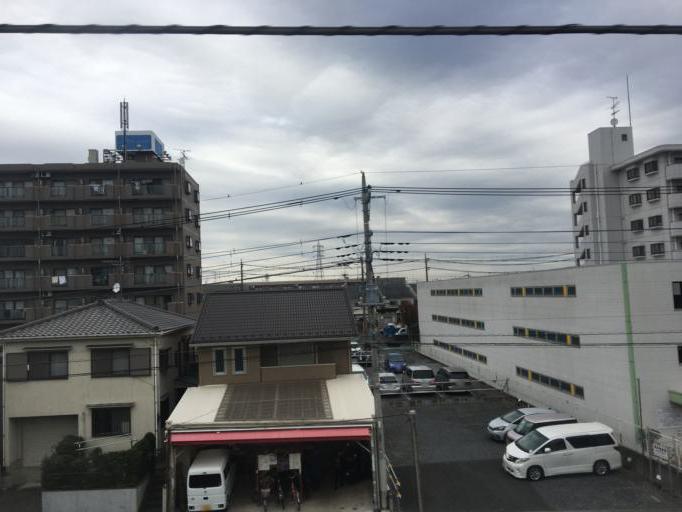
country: JP
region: Saitama
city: Yoshikawa
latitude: 35.8763
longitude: 139.8452
